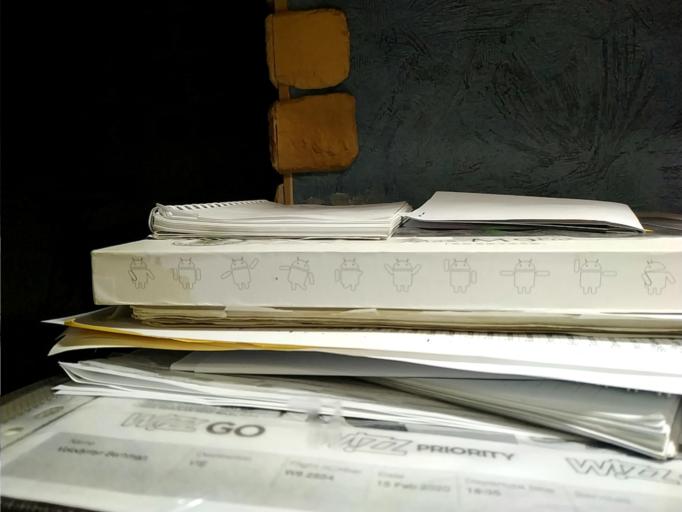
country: RU
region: Arkhangelskaya
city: Konevo
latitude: 62.8252
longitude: 38.5430
